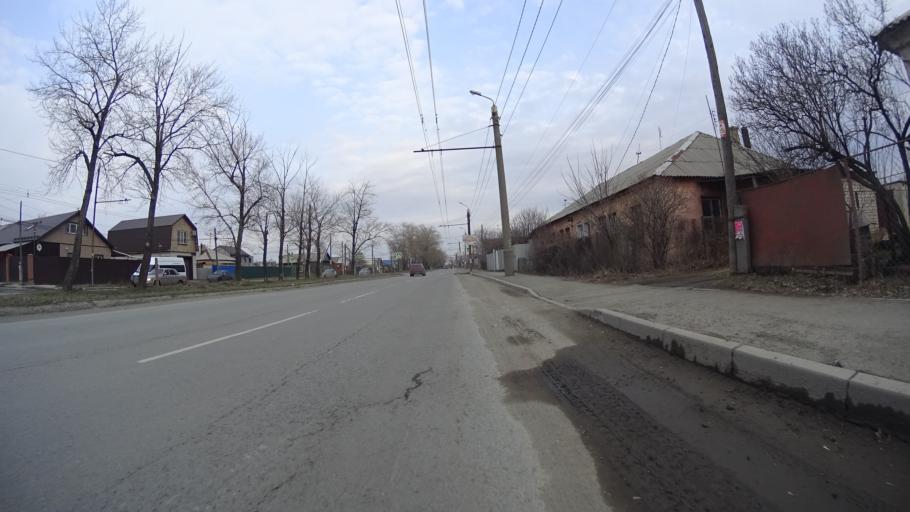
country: RU
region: Chelyabinsk
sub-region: Gorod Chelyabinsk
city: Chelyabinsk
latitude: 55.1921
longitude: 61.4689
